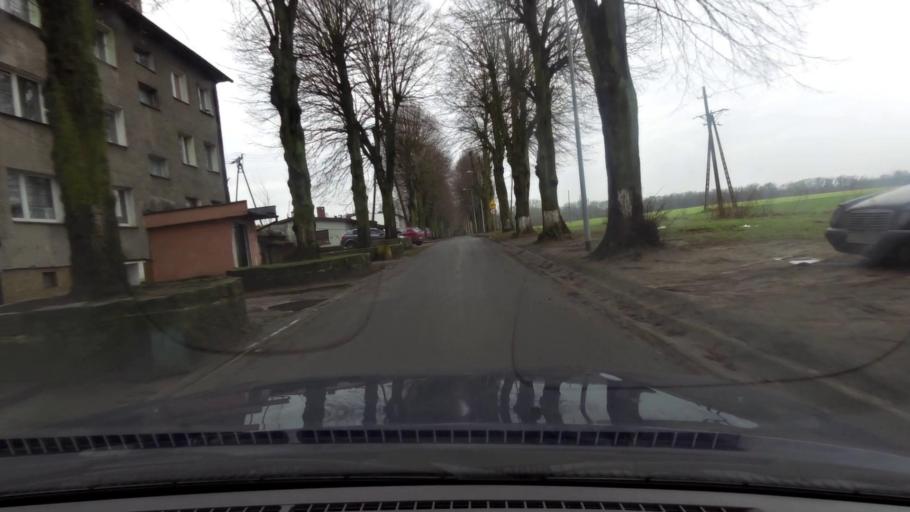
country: PL
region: West Pomeranian Voivodeship
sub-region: Powiat stargardzki
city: Stargard Szczecinski
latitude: 53.3314
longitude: 15.1394
